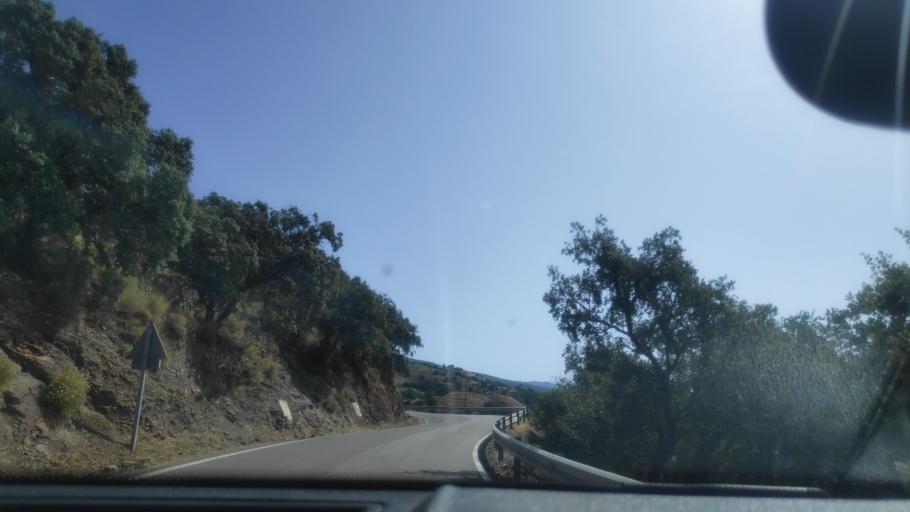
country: ES
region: Andalusia
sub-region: Provincia de Granada
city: Pampaneira
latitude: 36.9261
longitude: -3.3488
